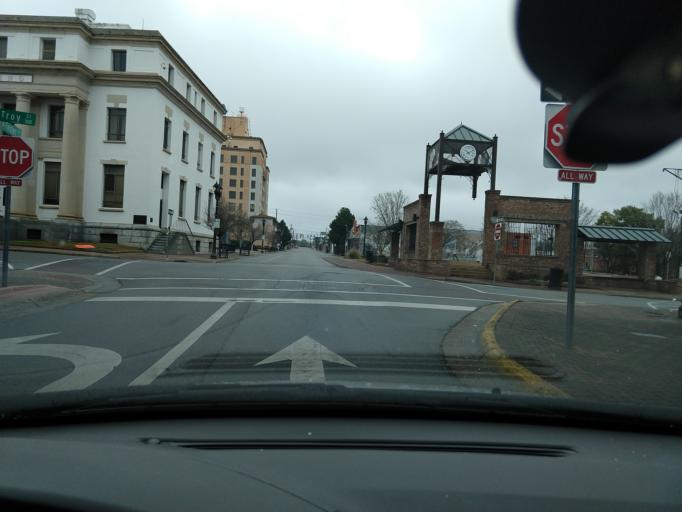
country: US
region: Alabama
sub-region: Houston County
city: Dothan
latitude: 31.2250
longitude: -85.3923
